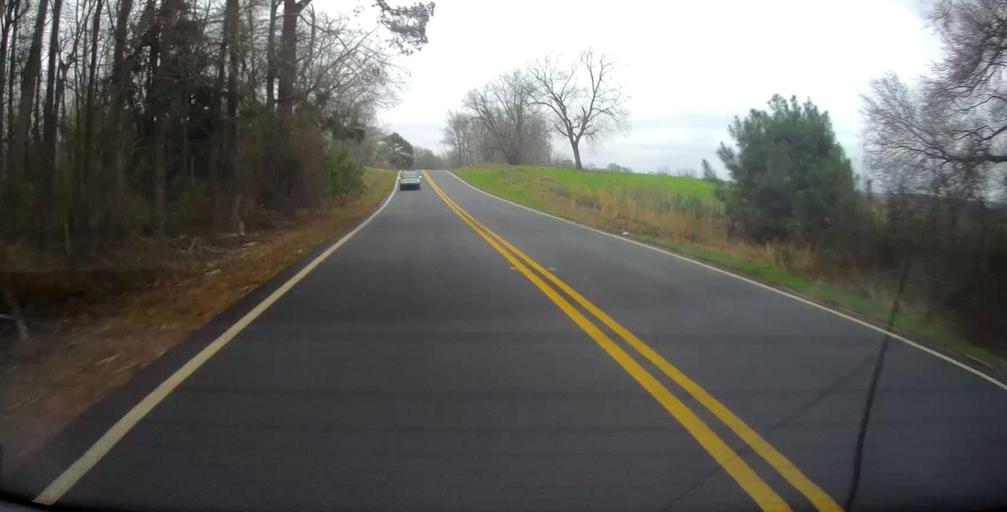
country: US
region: Georgia
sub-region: Pike County
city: Zebulon
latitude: 33.0514
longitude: -84.3005
